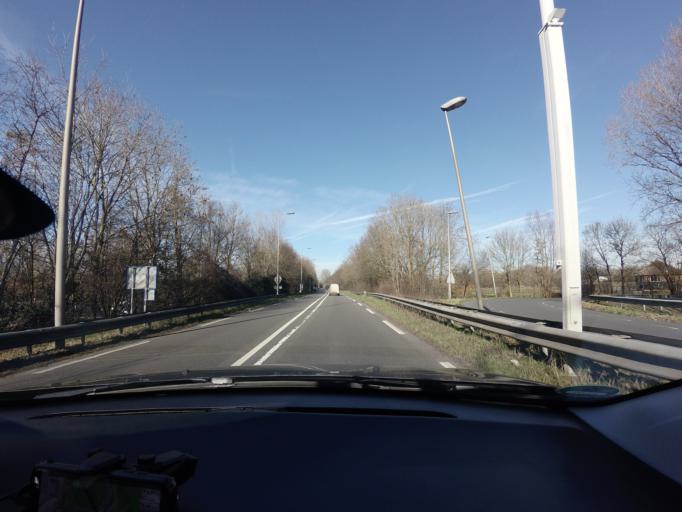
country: NL
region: South Holland
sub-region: Gemeente Alphen aan den Rijn
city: Alphen aan den Rijn
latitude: 52.1433
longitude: 4.7018
